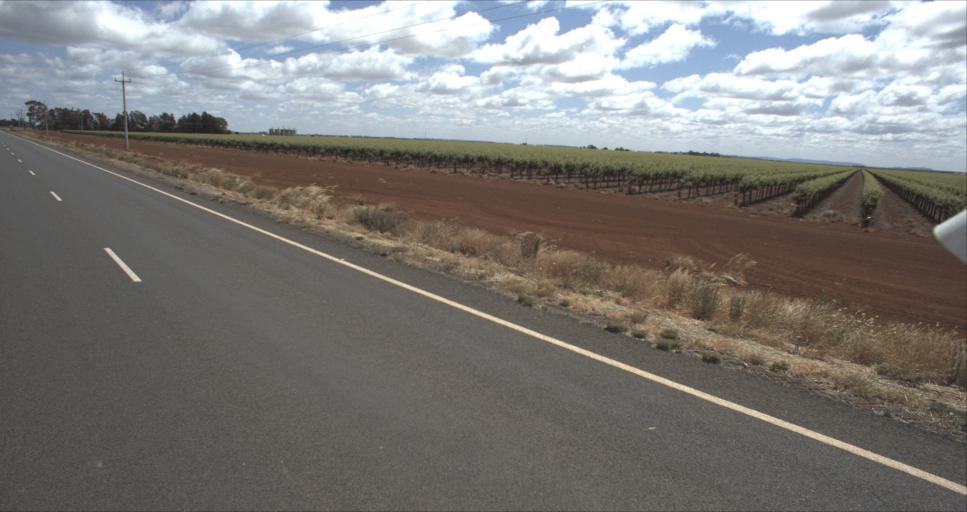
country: AU
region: New South Wales
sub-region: Murrumbidgee Shire
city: Darlington Point
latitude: -34.4710
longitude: 146.1404
